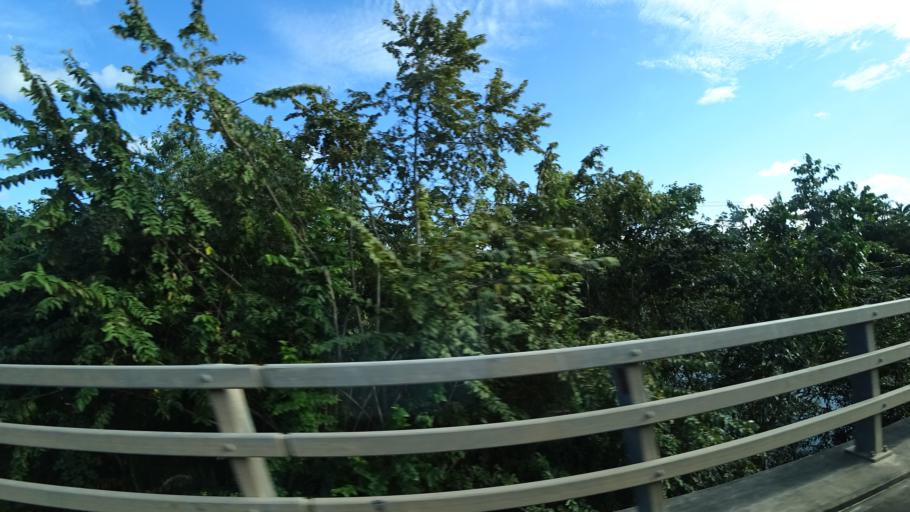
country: BZ
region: Belize
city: Belize City
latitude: 17.5706
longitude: -88.3862
